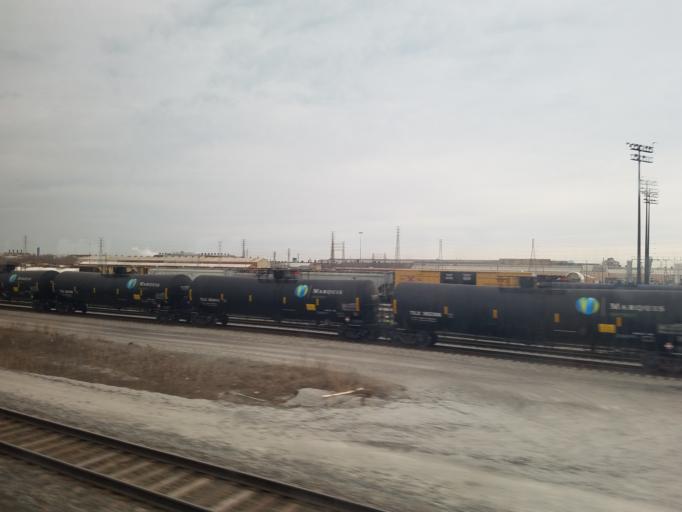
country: US
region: Indiana
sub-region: Lake County
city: Gary
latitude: 41.6119
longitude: -87.3578
